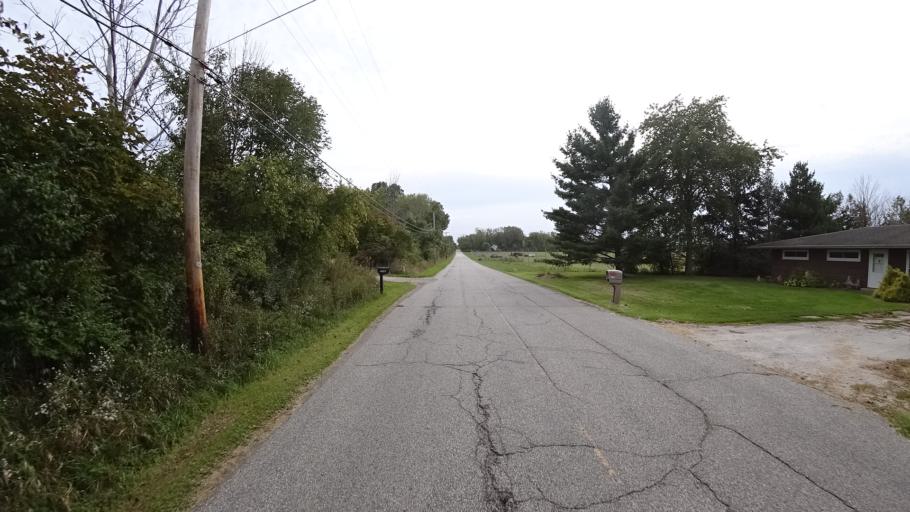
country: US
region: Indiana
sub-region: LaPorte County
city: Trail Creek
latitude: 41.7065
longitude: -86.8163
